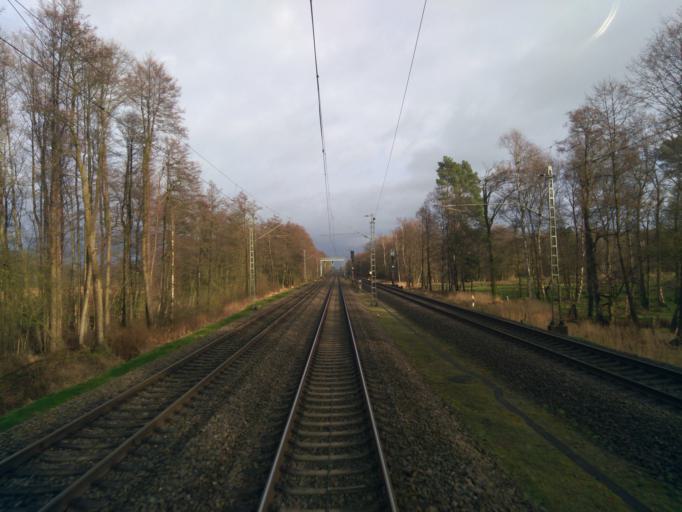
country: DE
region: Lower Saxony
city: Wistedt
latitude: 53.2474
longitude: 9.6787
